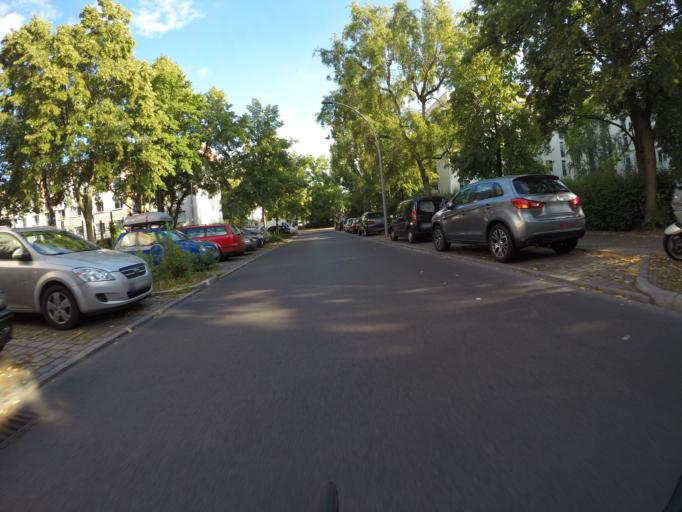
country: DE
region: Berlin
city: Weissensee
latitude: 52.5565
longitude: 13.4785
